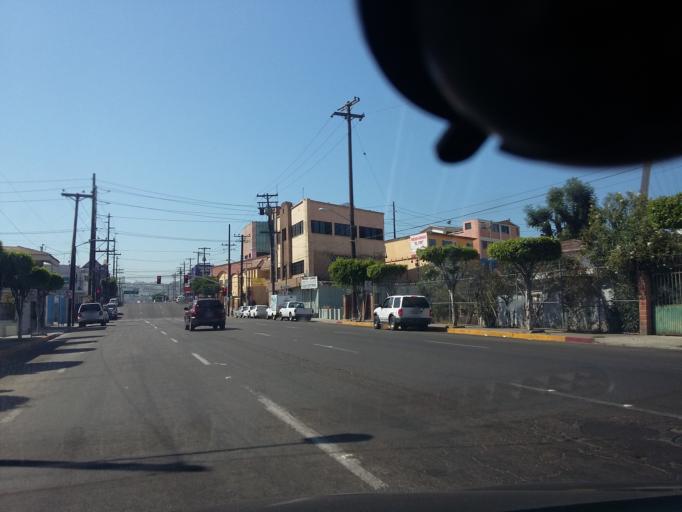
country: MX
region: Baja California
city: Tijuana
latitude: 32.5379
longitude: -117.0356
